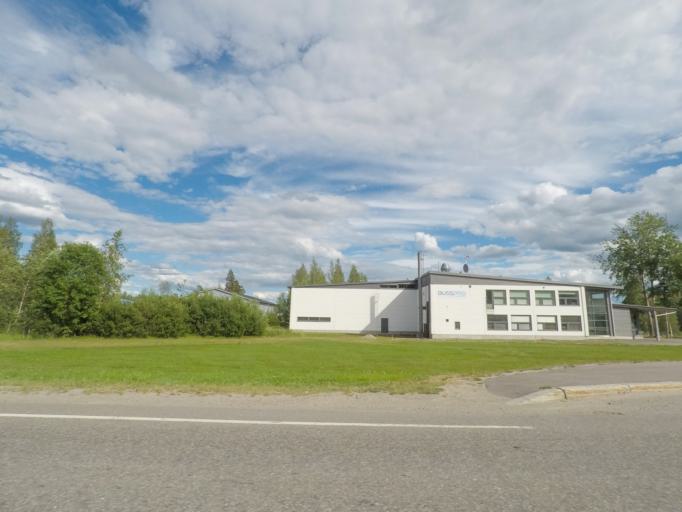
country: FI
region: Paijanne Tavastia
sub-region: Lahti
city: Lahti
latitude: 60.9358
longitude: 25.5908
